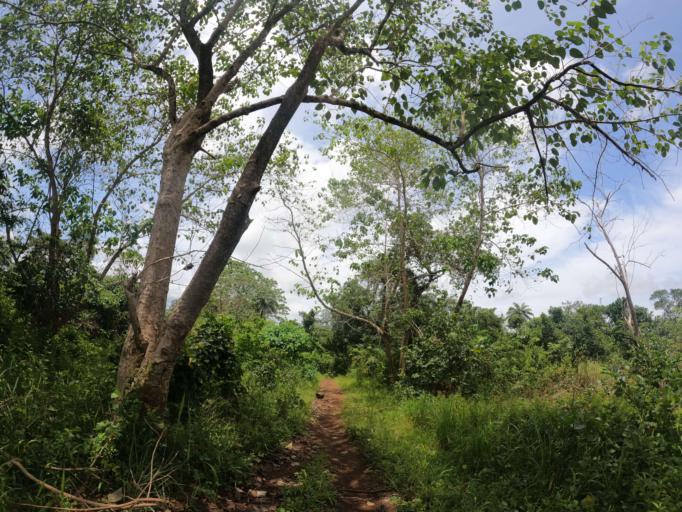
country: SL
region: Northern Province
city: Binkolo
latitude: 9.1475
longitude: -12.2460
